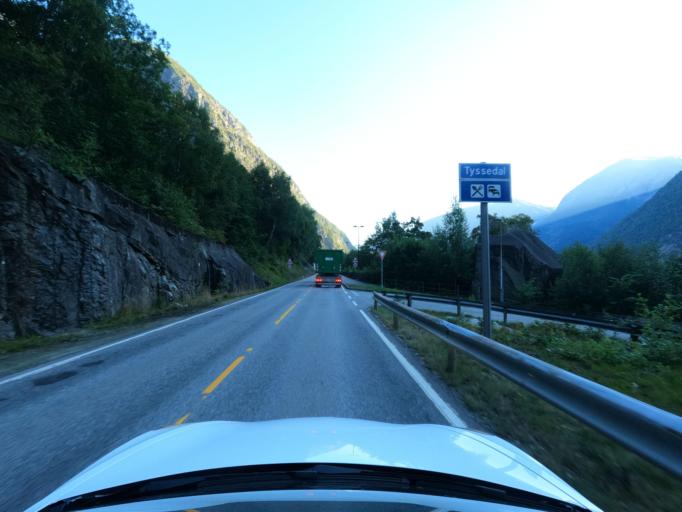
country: NO
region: Hordaland
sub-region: Odda
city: Odda
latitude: 60.1210
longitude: 6.5581
